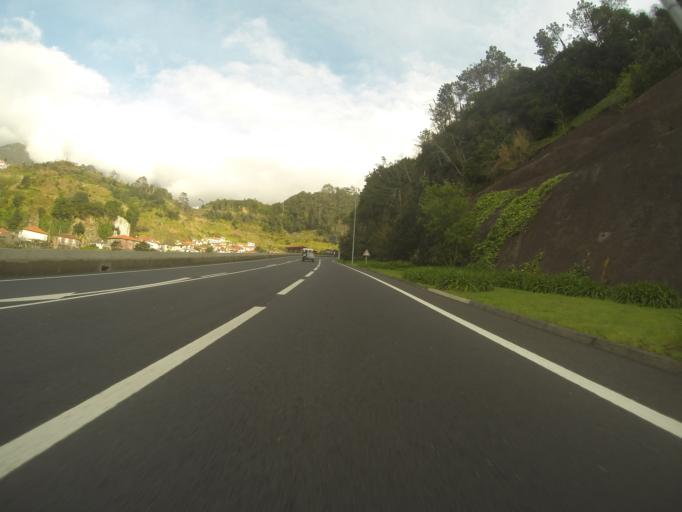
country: PT
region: Madeira
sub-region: Sao Vicente
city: Sao Vicente
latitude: 32.7725
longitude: -17.0307
